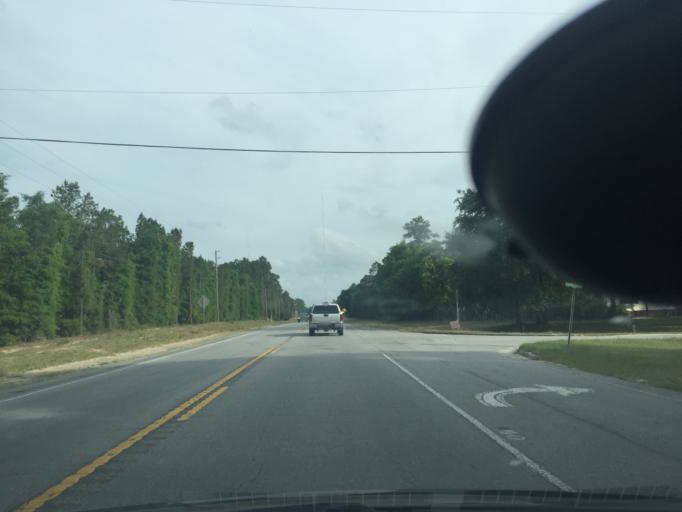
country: US
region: Georgia
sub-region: Chatham County
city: Bloomingdale
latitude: 32.0704
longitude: -81.3596
